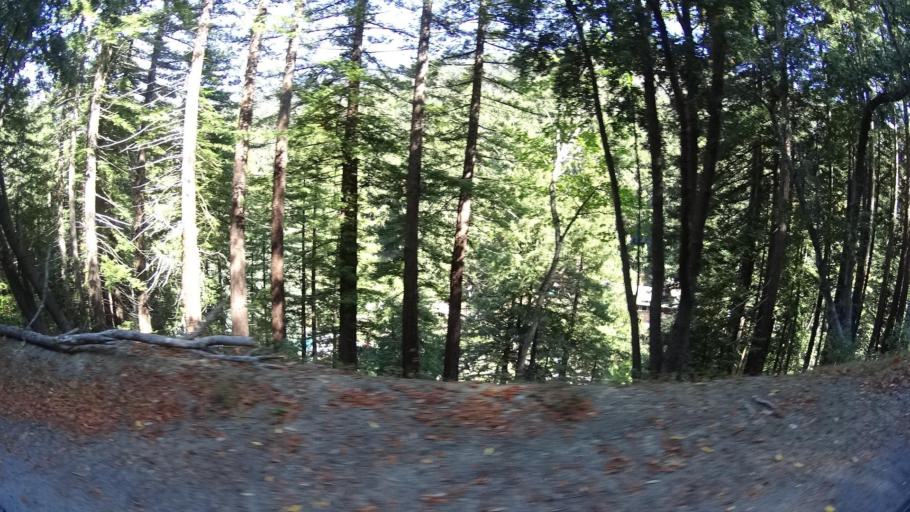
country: US
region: California
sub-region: Monterey County
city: Carmel Valley Village
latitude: 36.3800
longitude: -121.8620
